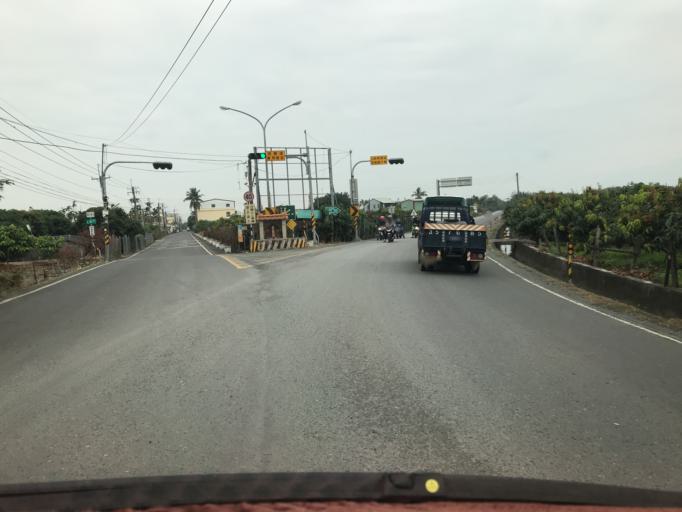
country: TW
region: Taiwan
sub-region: Pingtung
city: Pingtung
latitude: 22.5031
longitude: 120.5882
